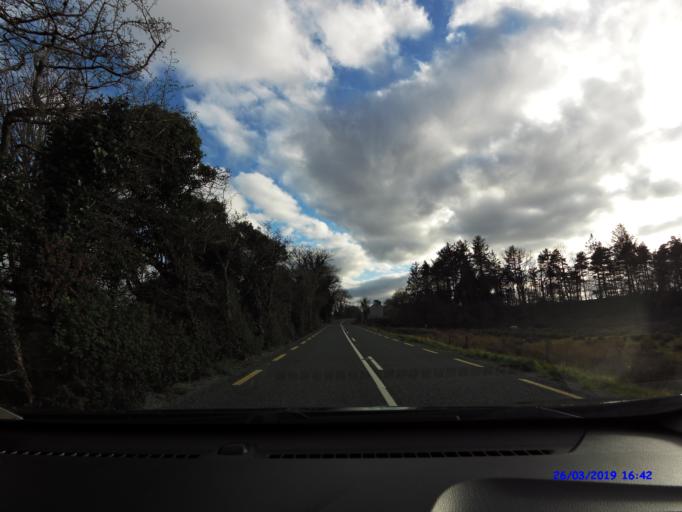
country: IE
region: Connaught
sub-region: Maigh Eo
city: Ballyhaunis
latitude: 53.8620
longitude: -8.7644
